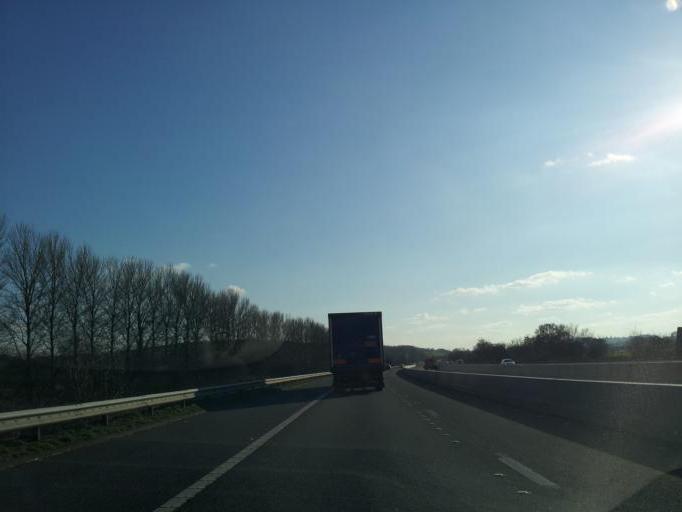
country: GB
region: England
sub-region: Devon
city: Bradninch
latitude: 50.8280
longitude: -3.4005
